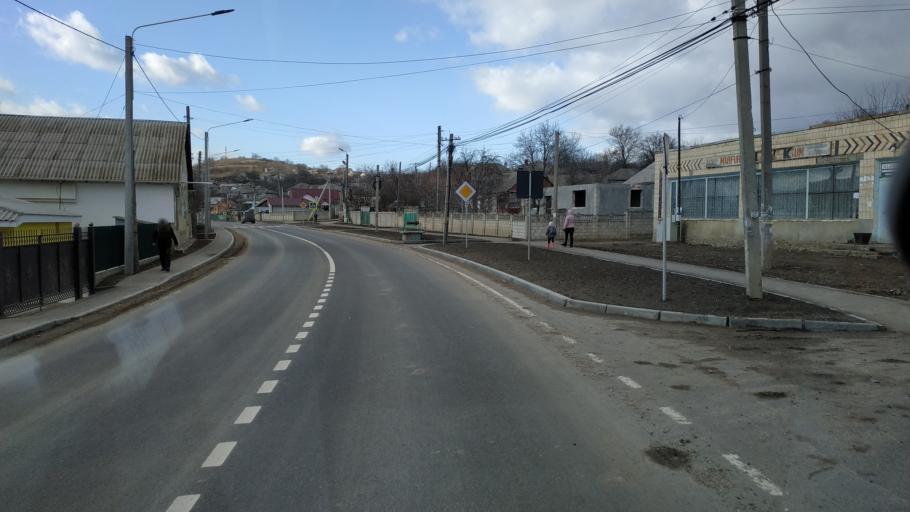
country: MD
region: Calarasi
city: Calarasi
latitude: 47.2884
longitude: 28.1954
